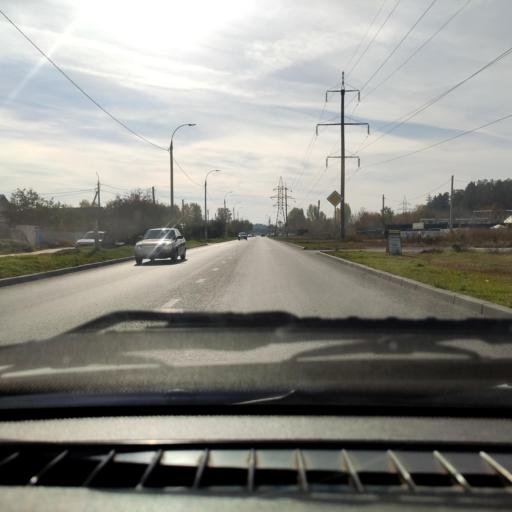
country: RU
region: Samara
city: Tol'yatti
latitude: 53.5167
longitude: 49.3955
